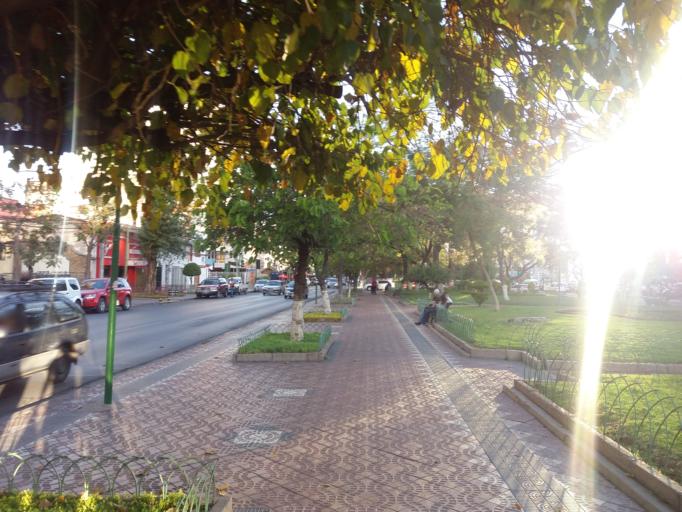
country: BO
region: Cochabamba
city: Cochabamba
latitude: -17.3832
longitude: -66.1591
